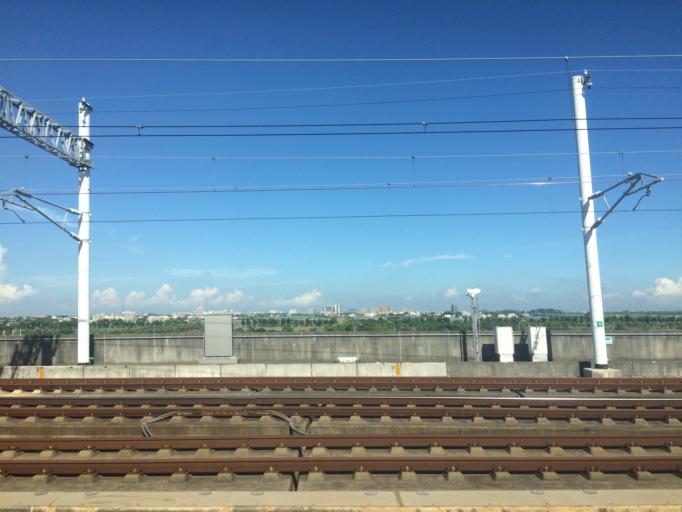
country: TW
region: Taiwan
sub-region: Chiayi
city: Taibao
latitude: 23.4641
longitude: 120.3241
